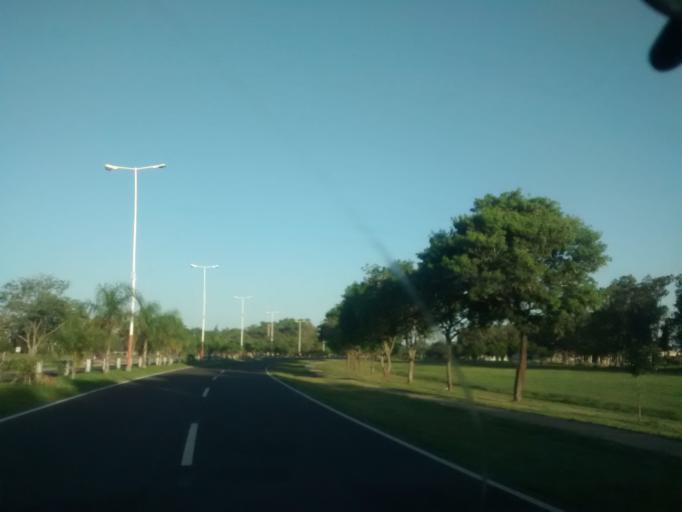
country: AR
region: Chaco
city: Fontana
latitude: -27.4410
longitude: -59.0291
